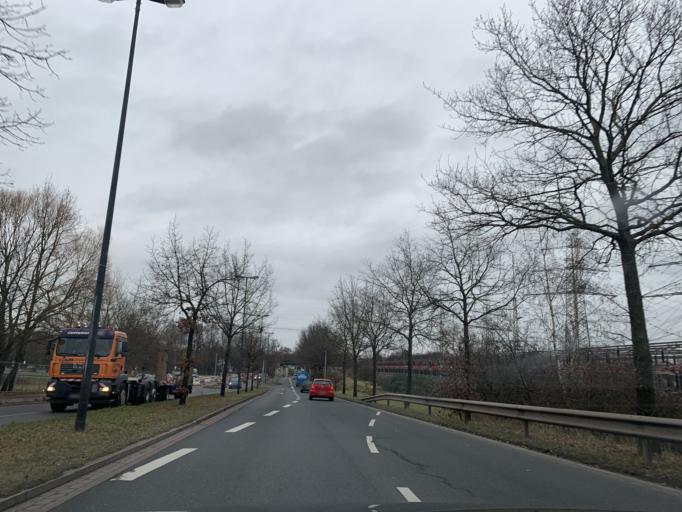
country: DE
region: Lower Saxony
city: Ritterhude
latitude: 53.1385
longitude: 8.7142
